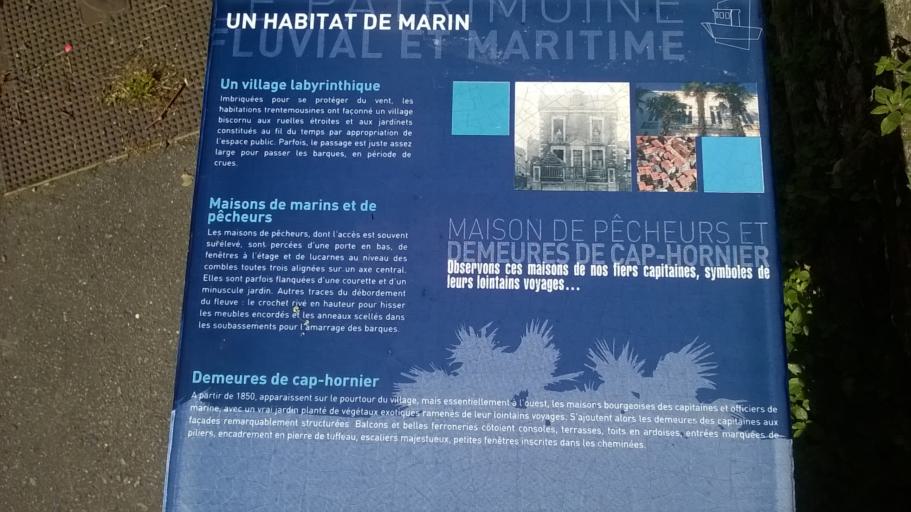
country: FR
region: Pays de la Loire
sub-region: Departement de la Loire-Atlantique
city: Reze
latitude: 47.1932
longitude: -1.5837
